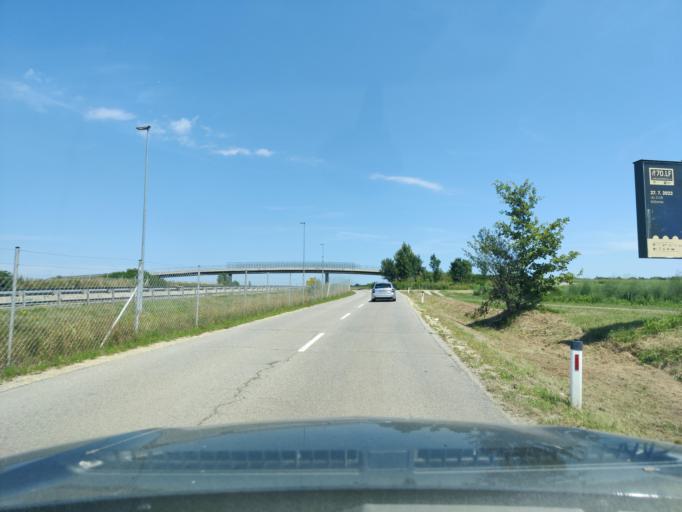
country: SI
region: Lendava-Lendva
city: Lendava
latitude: 46.5895
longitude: 16.4541
